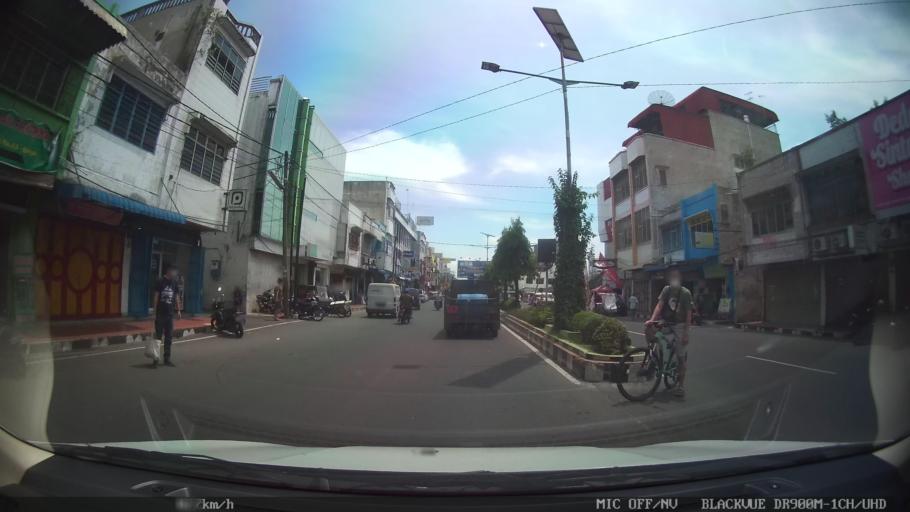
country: ID
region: North Sumatra
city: Binjai
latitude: 3.6044
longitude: 98.4846
